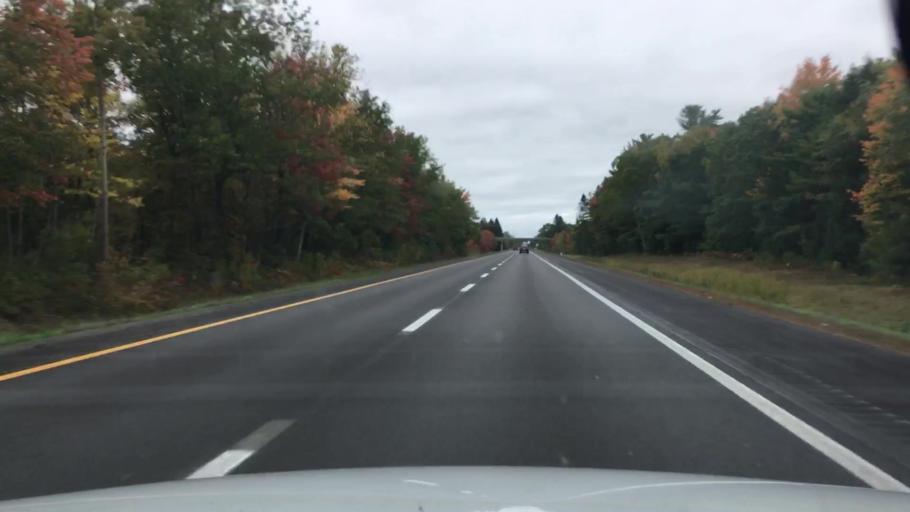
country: US
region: Maine
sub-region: Penobscot County
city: Veazie
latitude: 44.8418
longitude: -68.7336
